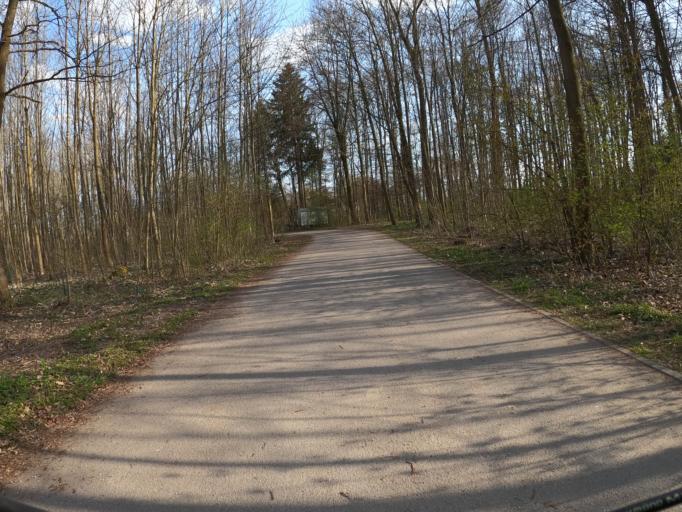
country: DE
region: Bavaria
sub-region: Swabia
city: Neu-Ulm
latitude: 48.4270
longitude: 10.0437
